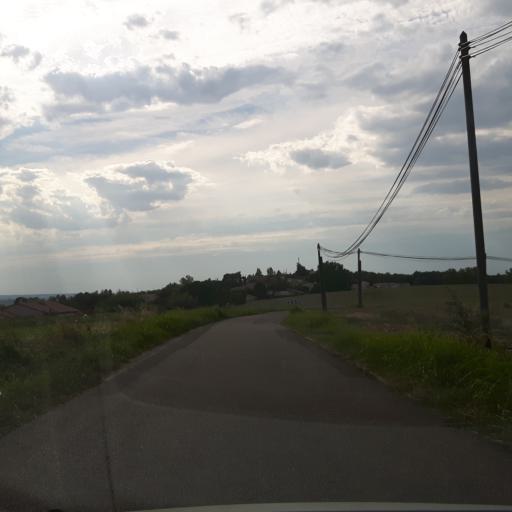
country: FR
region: Midi-Pyrenees
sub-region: Departement de la Haute-Garonne
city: Castelnau-d'Estretefonds
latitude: 43.7983
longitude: 1.3551
